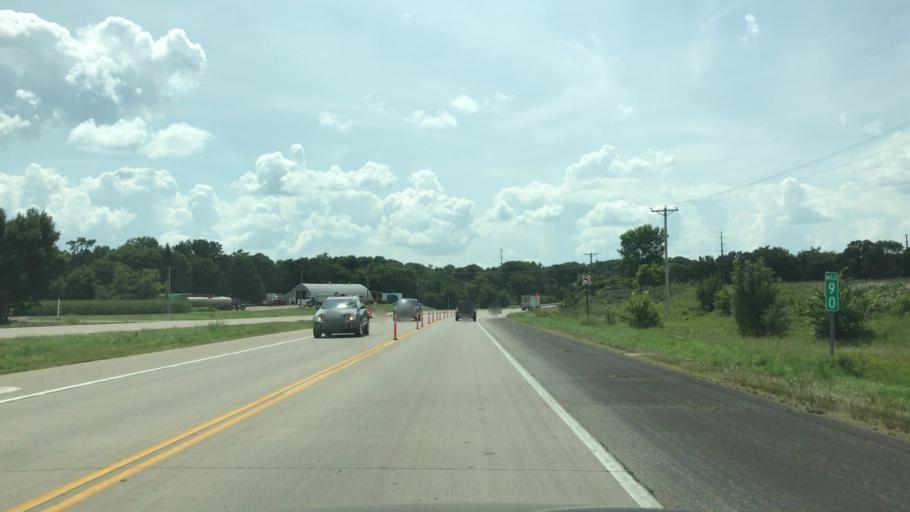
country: US
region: Minnesota
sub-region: Scott County
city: Belle Plaine
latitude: 44.6033
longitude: -93.7868
